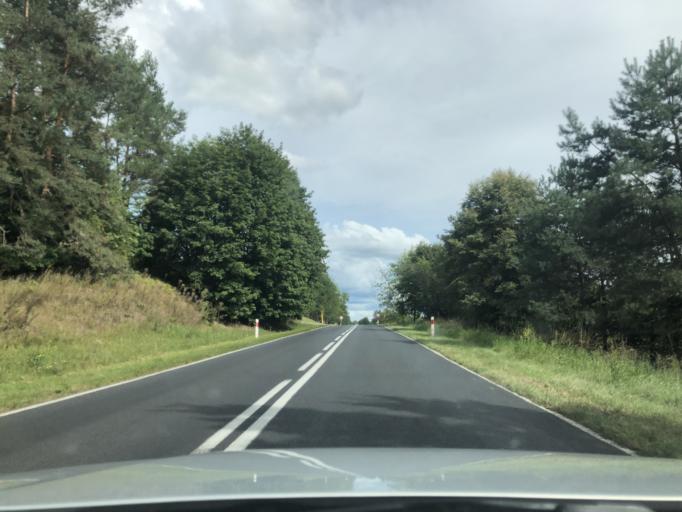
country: PL
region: Greater Poland Voivodeship
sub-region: Powiat pilski
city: Szydlowo
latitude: 53.0831
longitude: 16.6100
